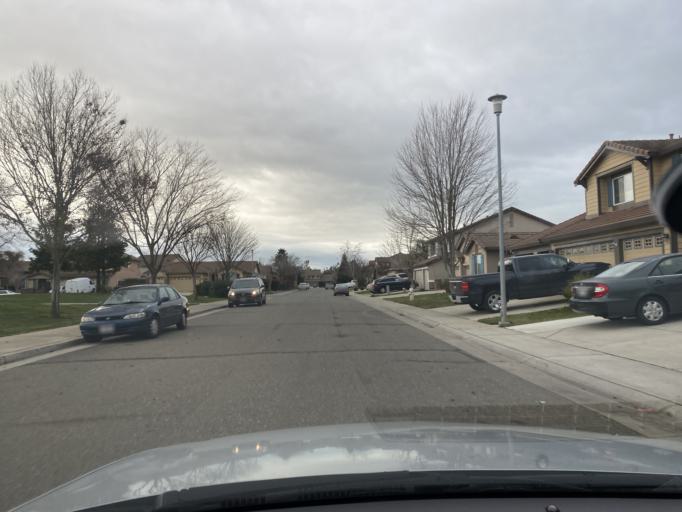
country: US
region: California
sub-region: Sacramento County
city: Elk Grove
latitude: 38.4426
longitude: -121.3897
